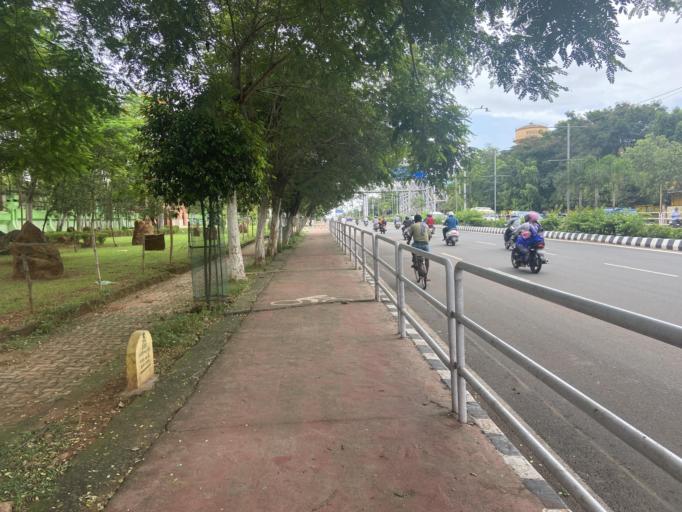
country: IN
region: Odisha
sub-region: Khordha
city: Bhubaneshwar
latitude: 20.2884
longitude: 85.8262
